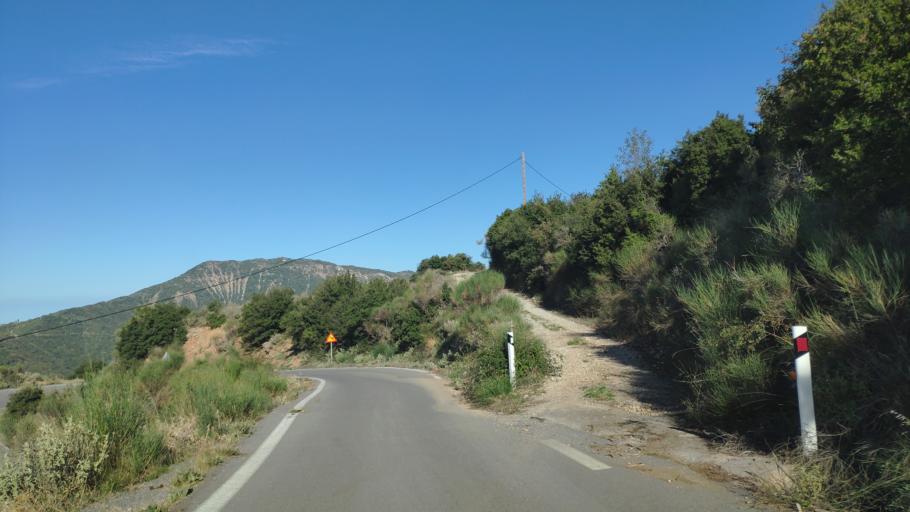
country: GR
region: Peloponnese
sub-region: Nomos Arkadias
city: Dimitsana
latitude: 37.5524
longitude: 22.0632
